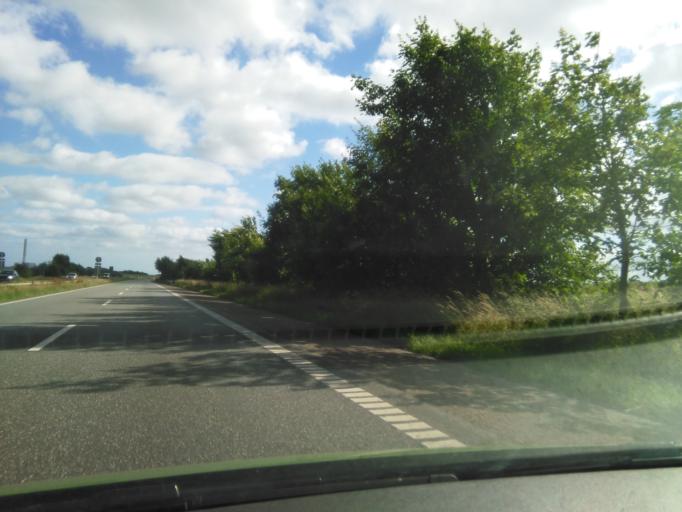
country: DK
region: Central Jutland
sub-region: Arhus Kommune
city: Logten
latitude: 56.2806
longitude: 10.3308
